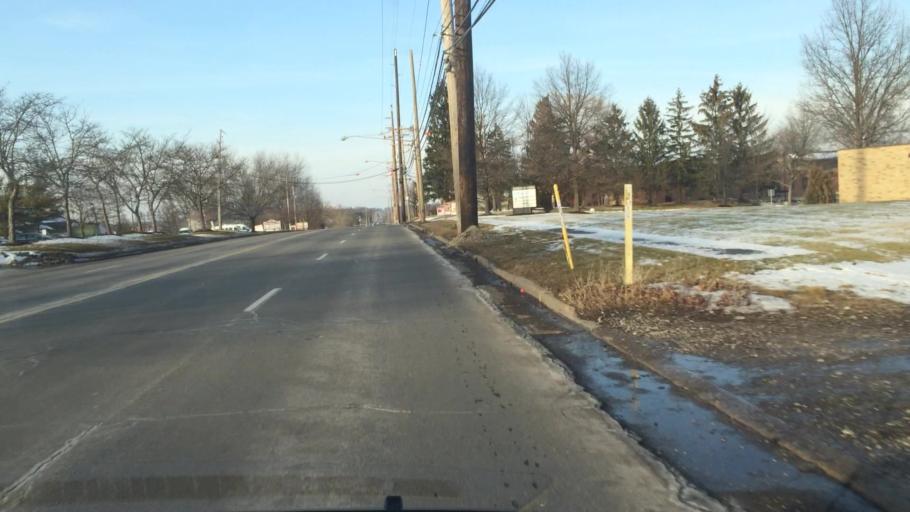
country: US
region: Ohio
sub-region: Summit County
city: Stow
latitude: 41.1862
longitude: -81.4404
